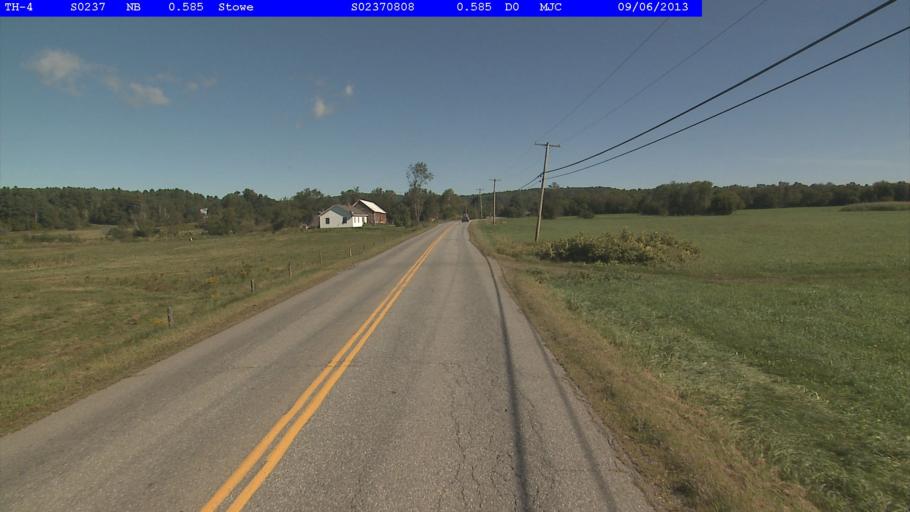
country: US
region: Vermont
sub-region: Lamoille County
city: Morristown
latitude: 44.4896
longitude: -72.6607
